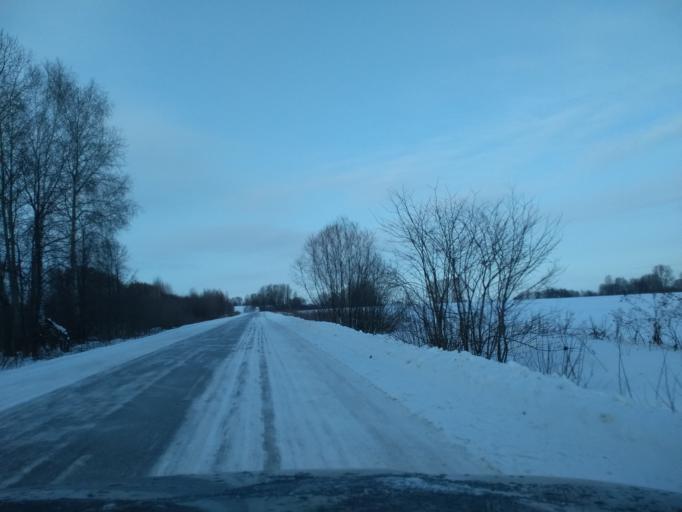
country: RU
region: Bashkortostan
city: Iglino
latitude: 54.7522
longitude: 56.5867
